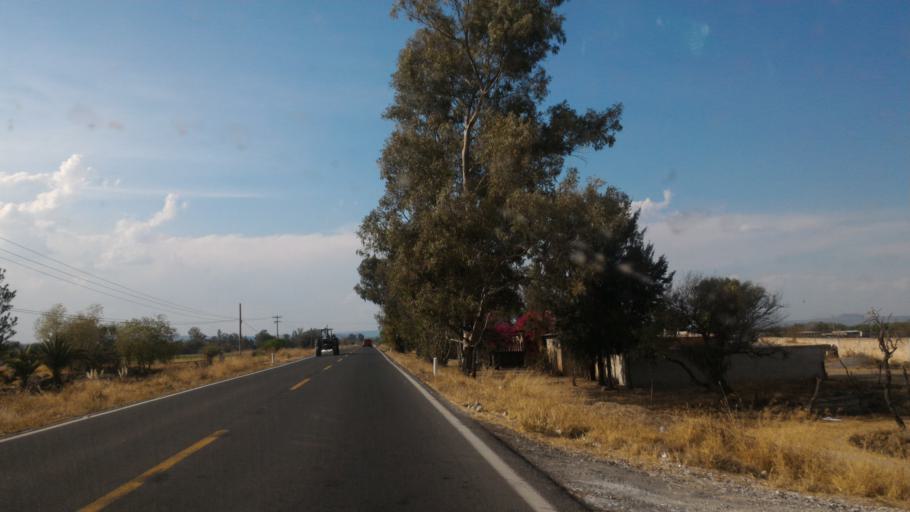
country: MX
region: Guanajuato
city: Ciudad Manuel Doblado
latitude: 20.7749
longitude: -101.9754
